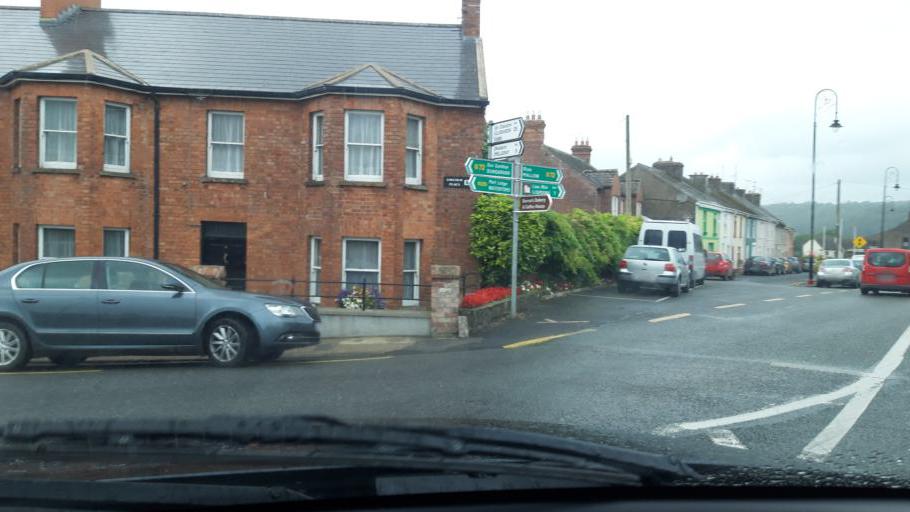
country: IE
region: Munster
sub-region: County Cork
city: Youghal
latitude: 52.1461
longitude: -7.8498
